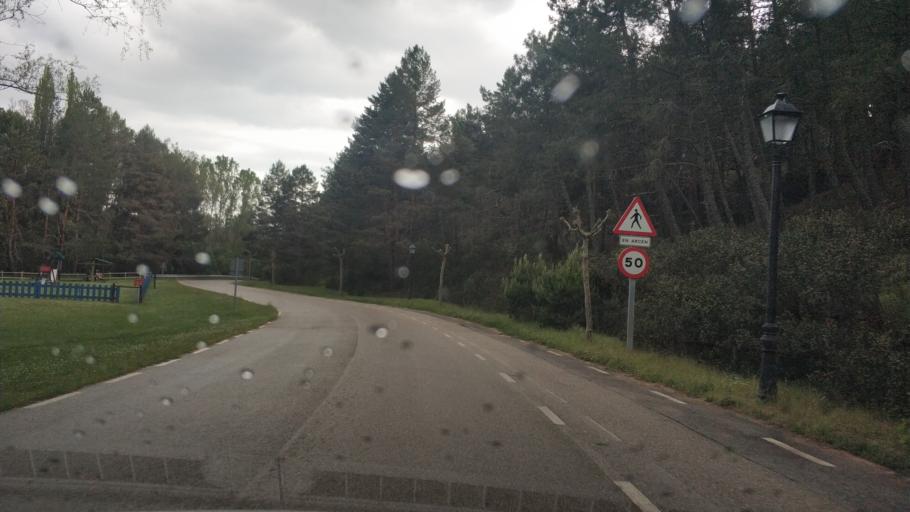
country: ES
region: Castille and Leon
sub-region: Provincia de Soria
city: San Leonardo de Yague
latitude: 41.8370
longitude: -3.0661
